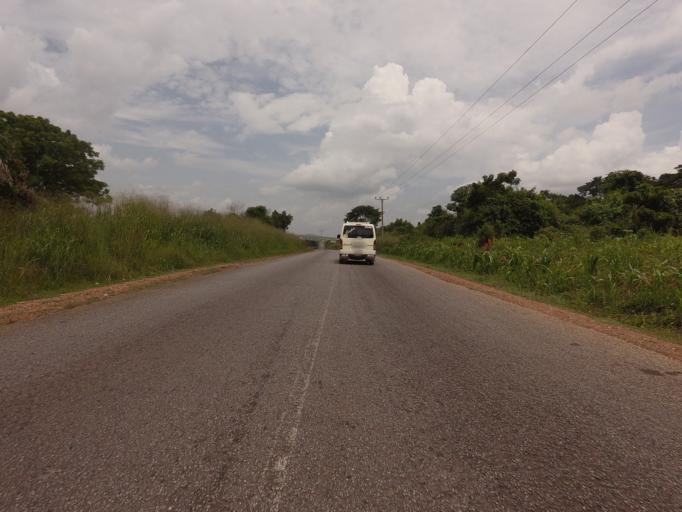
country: GH
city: Akropong
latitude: 6.2756
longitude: 0.1335
